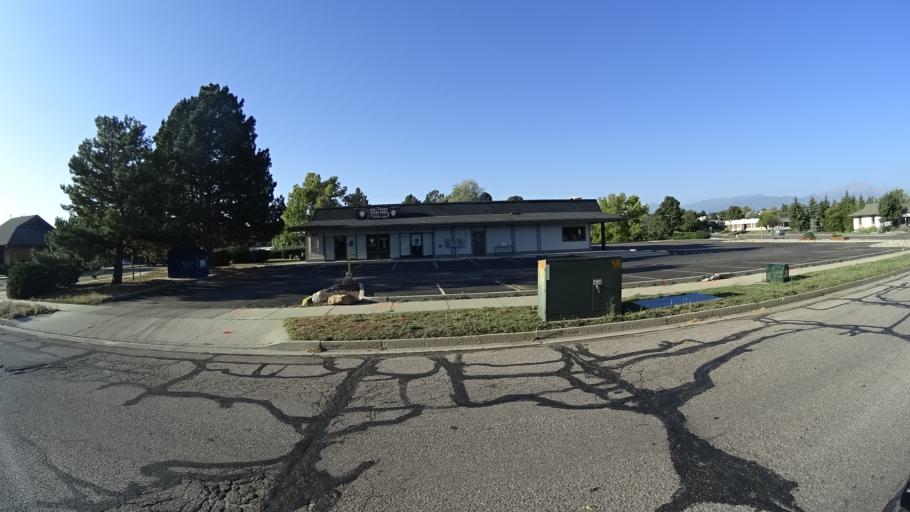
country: US
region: Colorado
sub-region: El Paso County
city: Cimarron Hills
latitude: 38.8804
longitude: -104.7529
